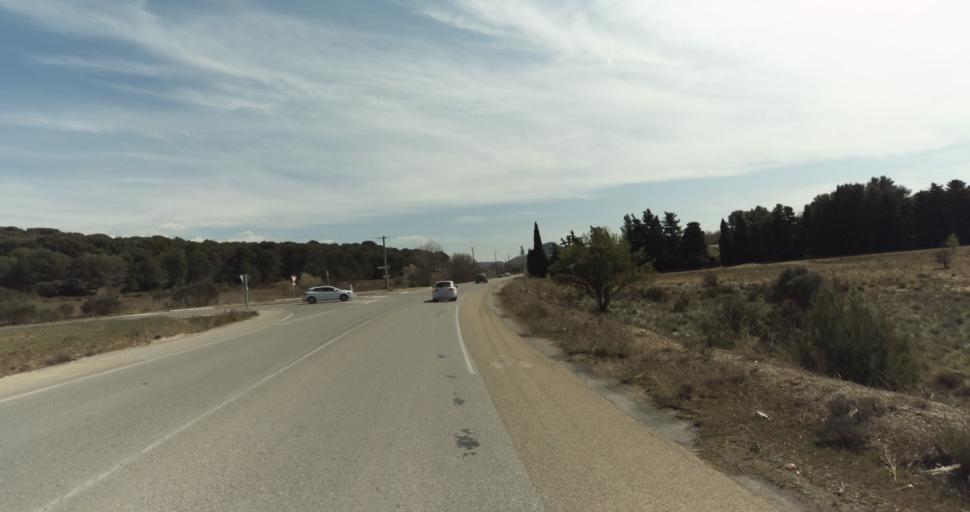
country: FR
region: Provence-Alpes-Cote d'Azur
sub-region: Departement des Bouches-du-Rhone
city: Coudoux
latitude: 43.5454
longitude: 5.2564
